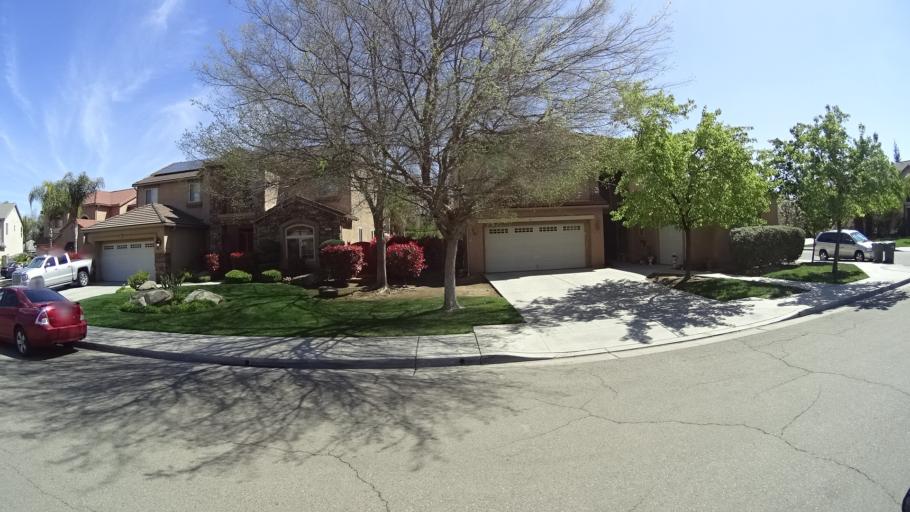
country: US
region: California
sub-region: Fresno County
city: Biola
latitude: 36.8207
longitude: -119.9123
